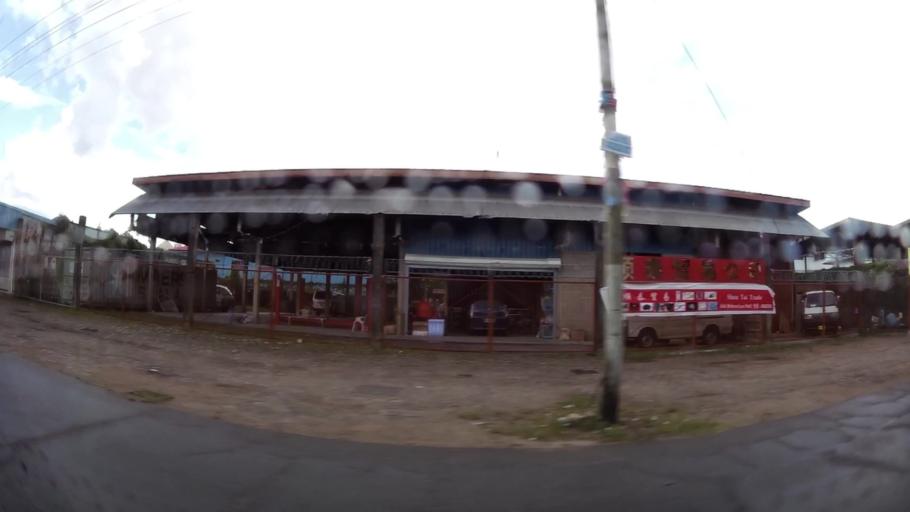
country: SR
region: Paramaribo
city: Paramaribo
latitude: 5.8345
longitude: -55.1457
